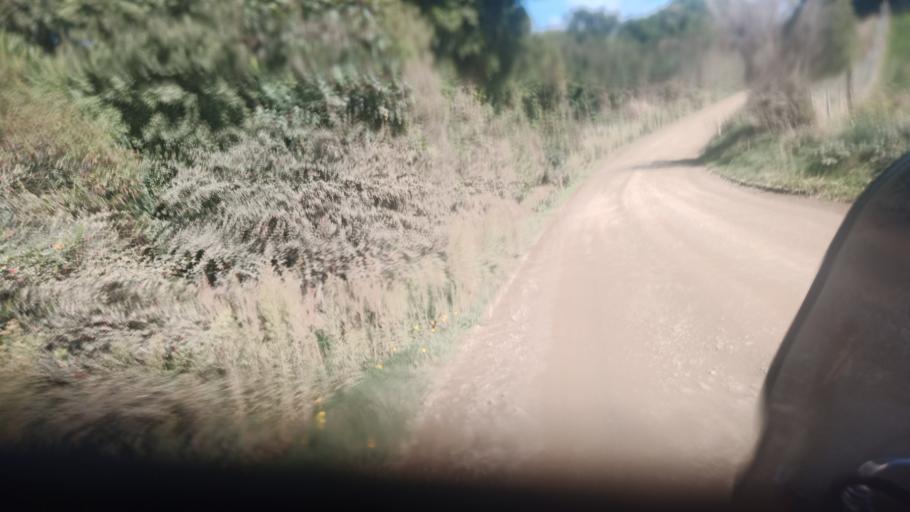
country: NZ
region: Bay of Plenty
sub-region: Opotiki District
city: Opotiki
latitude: -38.4364
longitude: 177.5458
